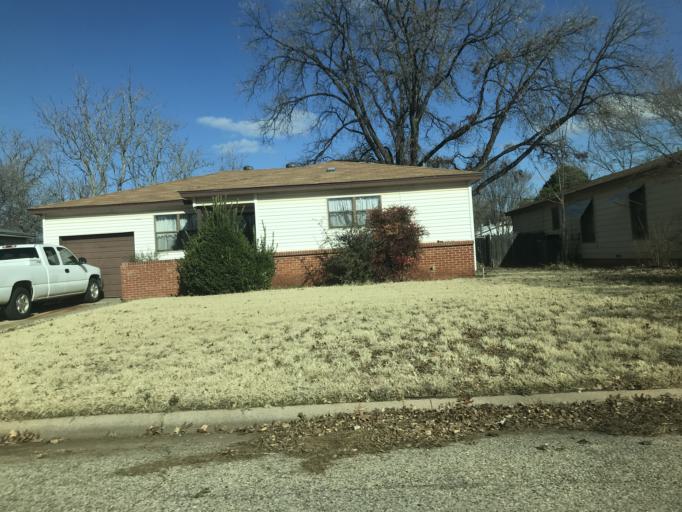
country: US
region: Texas
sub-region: Taylor County
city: Abilene
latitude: 32.4618
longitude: -99.7702
